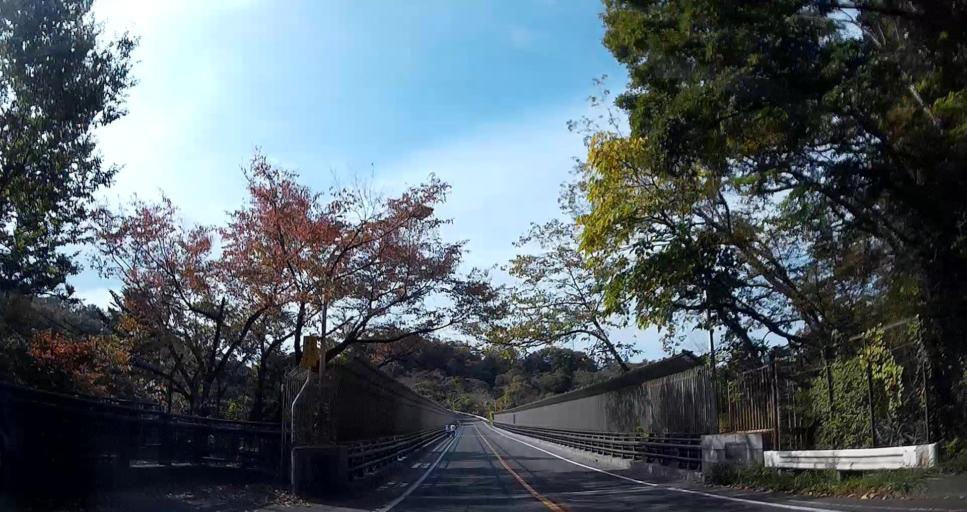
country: JP
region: Miyagi
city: Sendai
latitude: 38.2507
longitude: 140.8529
